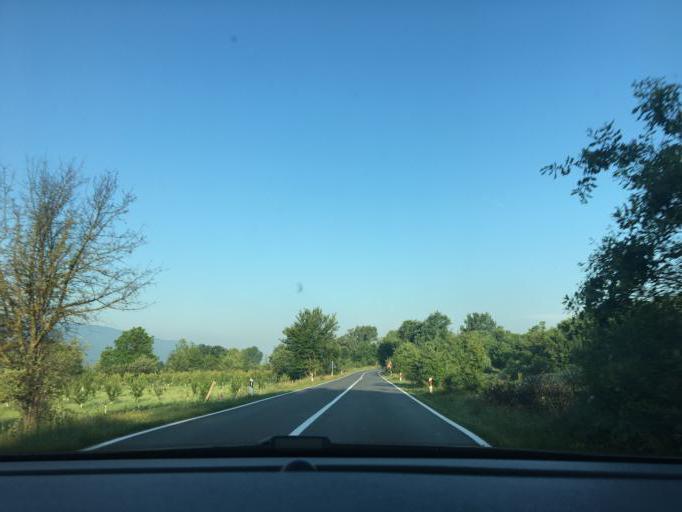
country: MK
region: Novo Selo
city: Novo Selo
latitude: 41.4021
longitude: 22.8871
